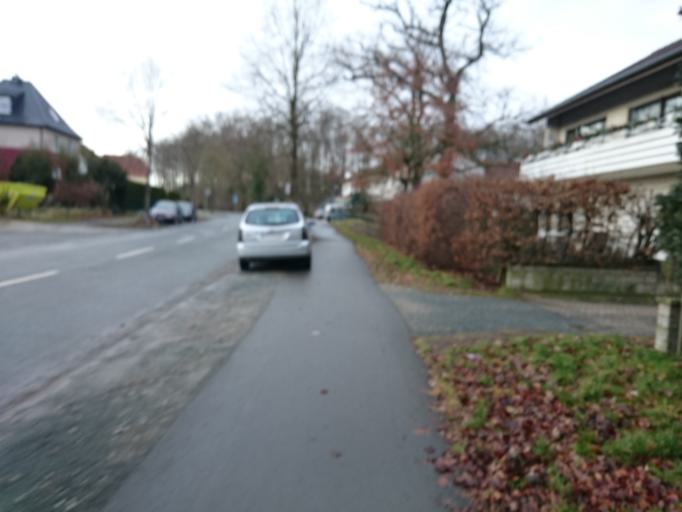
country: DE
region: North Rhine-Westphalia
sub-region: Regierungsbezirk Detmold
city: Lage
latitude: 52.0005
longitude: 8.8014
